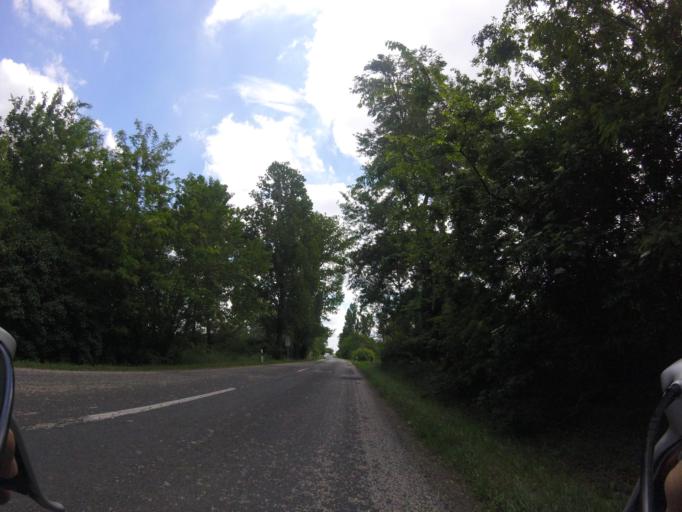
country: HU
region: Fejer
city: Sarosd
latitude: 47.0698
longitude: 18.6174
